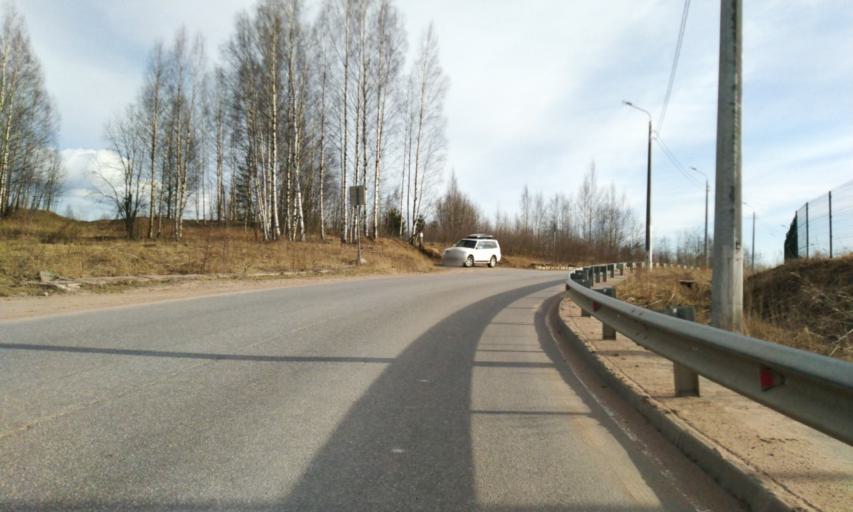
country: RU
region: Leningrad
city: Bugry
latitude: 60.1183
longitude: 30.4280
